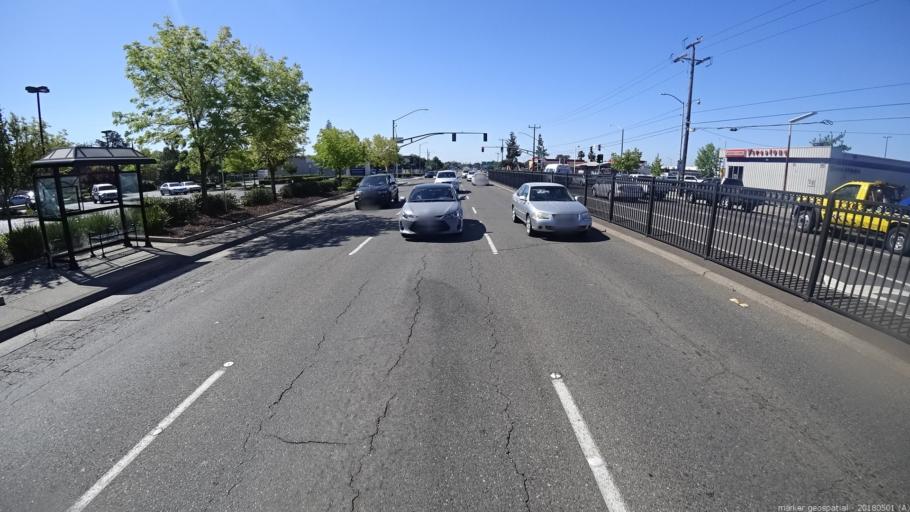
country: US
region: California
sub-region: Sacramento County
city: North Highlands
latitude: 38.6497
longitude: -121.3829
